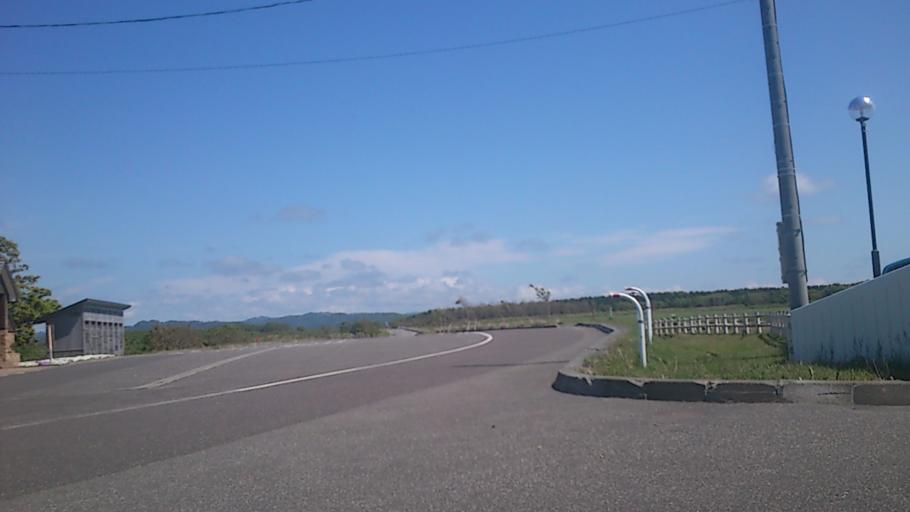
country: JP
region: Hokkaido
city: Rumoi
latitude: 44.5627
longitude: 141.7744
